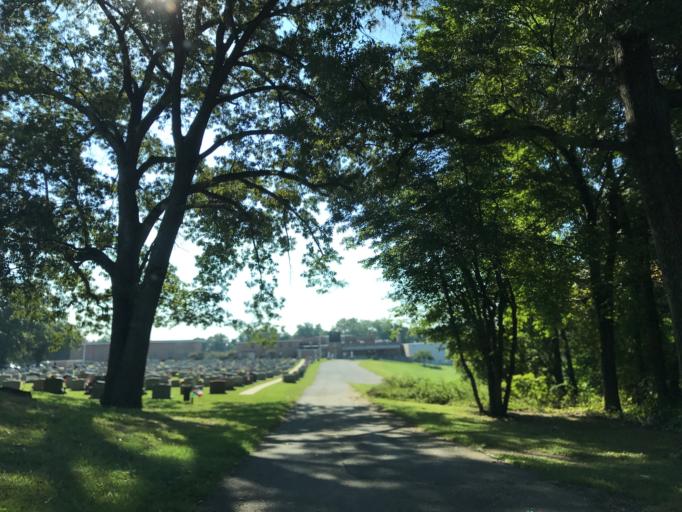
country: US
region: Maryland
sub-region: Baltimore County
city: Carney
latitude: 39.3881
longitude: -76.4986
